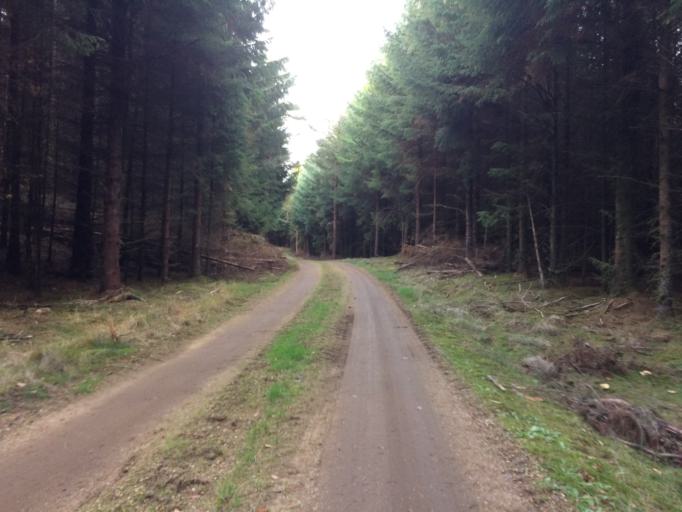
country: DK
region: Central Jutland
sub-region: Holstebro Kommune
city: Ulfborg
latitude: 56.2119
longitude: 8.4670
